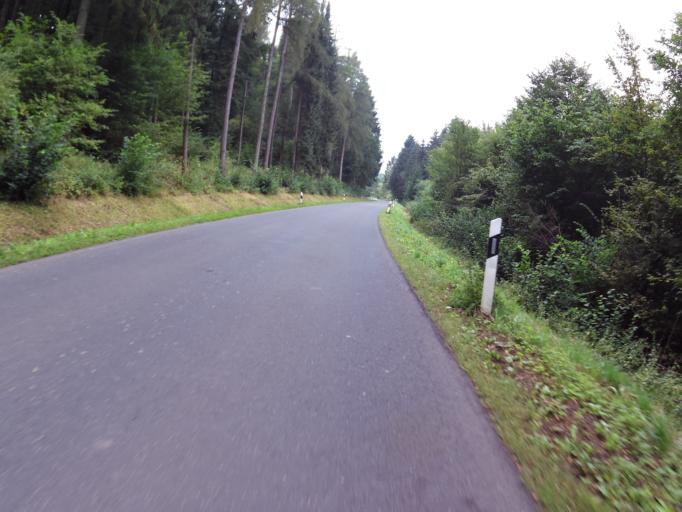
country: DE
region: Rheinland-Pfalz
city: Wilsecker
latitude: 50.0181
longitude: 6.5767
